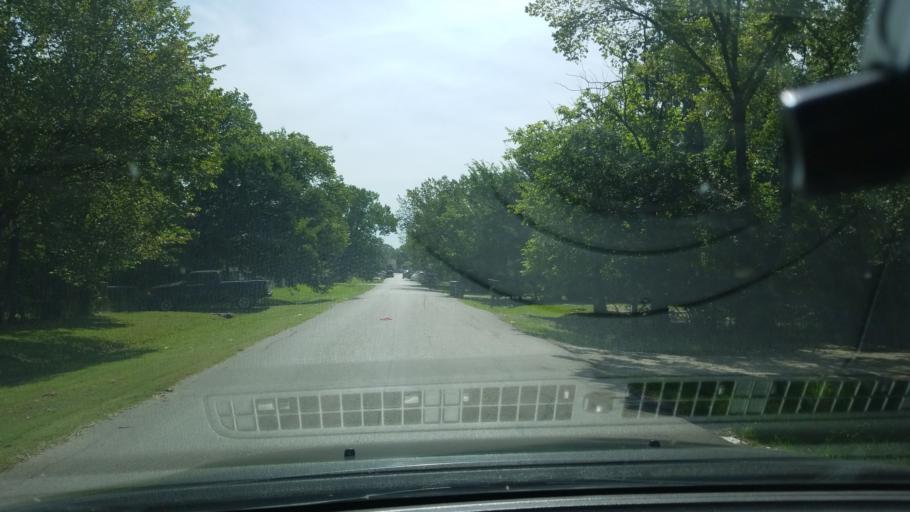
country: US
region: Texas
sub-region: Dallas County
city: Balch Springs
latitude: 32.7329
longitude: -96.6263
